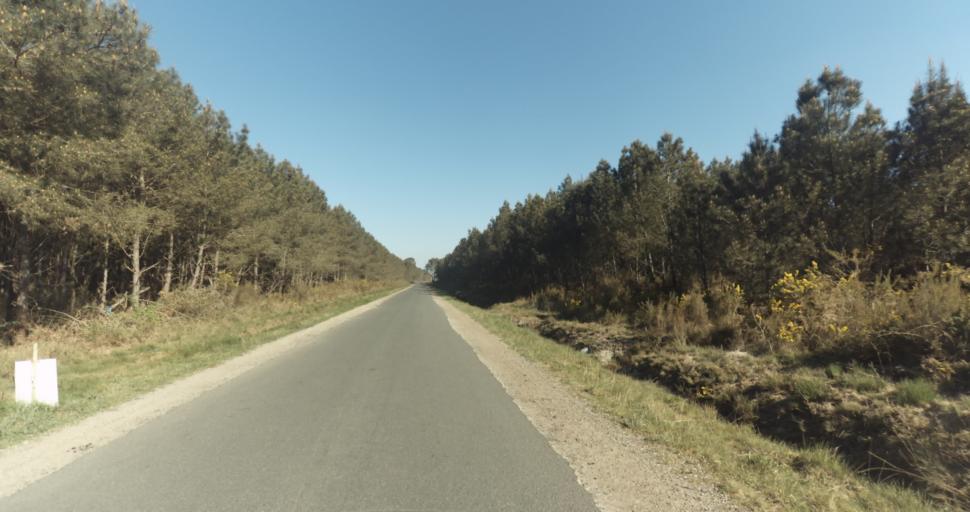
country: FR
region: Aquitaine
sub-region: Departement de la Gironde
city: Marcheprime
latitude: 44.7536
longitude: -0.8493
